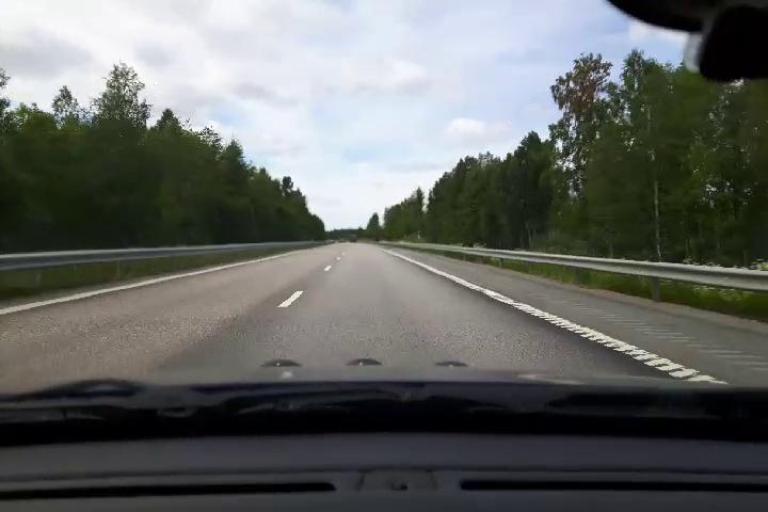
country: SE
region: Uppsala
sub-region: Alvkarleby Kommun
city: AElvkarleby
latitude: 60.4845
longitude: 17.3590
